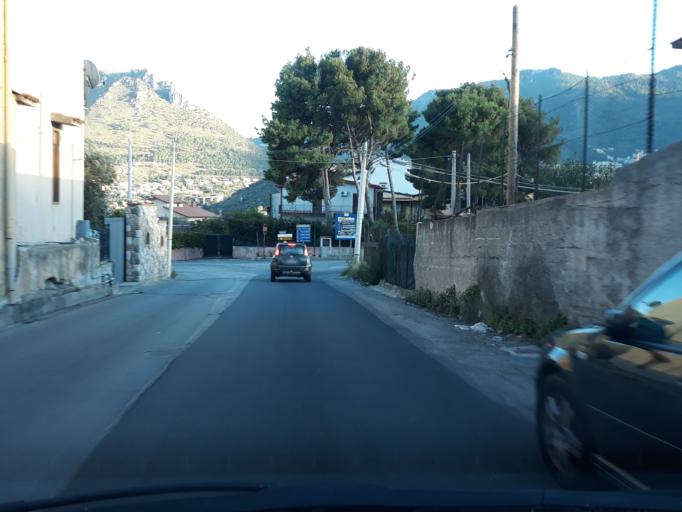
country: IT
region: Sicily
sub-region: Palermo
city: Monreale
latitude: 38.0719
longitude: 13.2966
